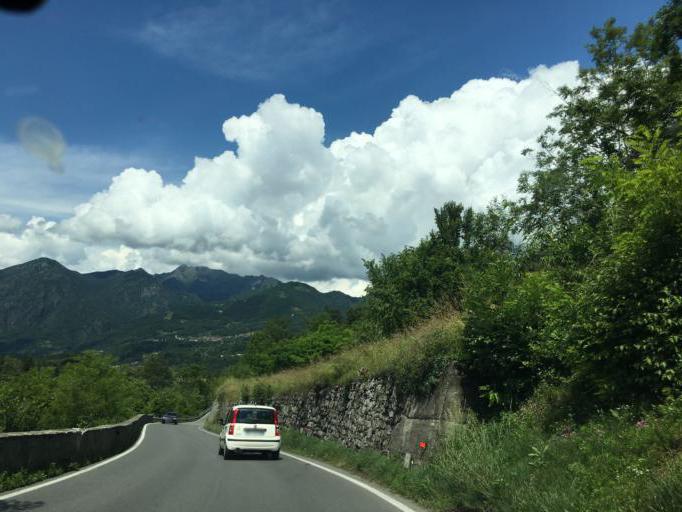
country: IT
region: Lombardy
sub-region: Provincia di Como
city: Bene Lario
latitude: 46.0373
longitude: 9.1819
